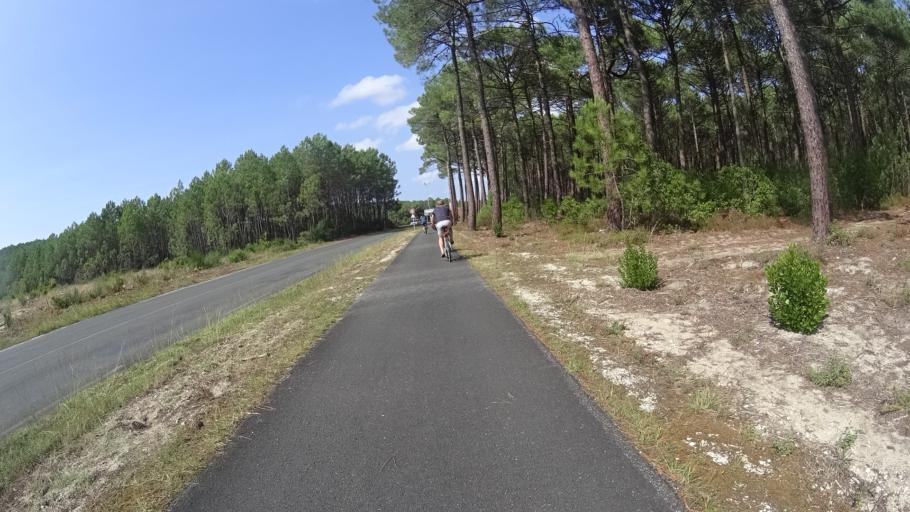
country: FR
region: Aquitaine
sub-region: Departement de la Gironde
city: Lacanau
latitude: 44.9846
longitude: -1.1439
